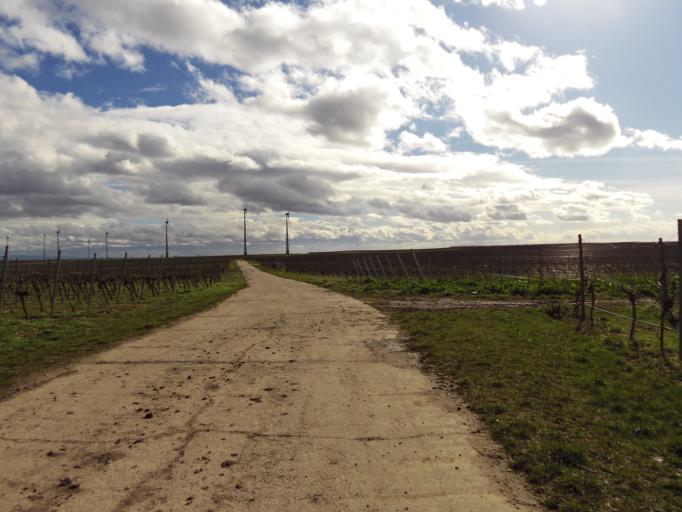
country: DE
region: Rheinland-Pfalz
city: Offstein
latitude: 49.5964
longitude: 8.2640
